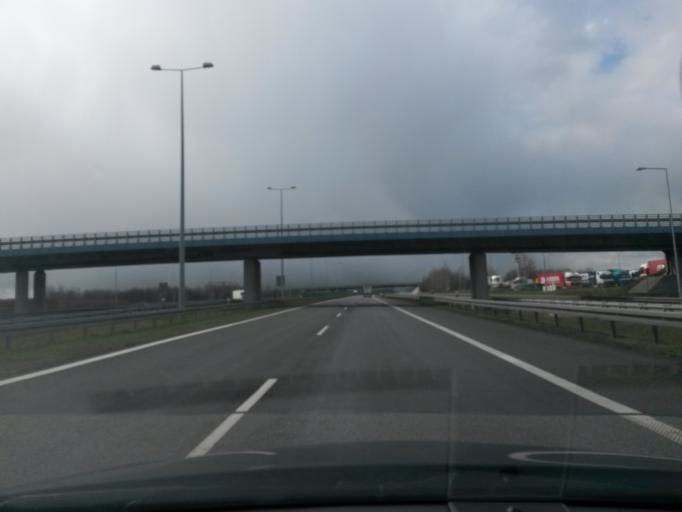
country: PL
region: Greater Poland Voivodeship
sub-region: Powiat koninski
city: Stare Miasto
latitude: 52.1624
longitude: 18.2129
